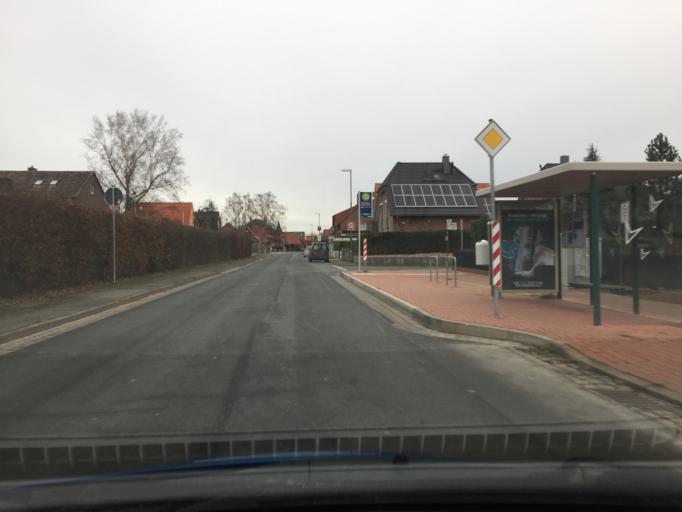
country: DE
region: Lower Saxony
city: Pattensen
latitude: 52.2879
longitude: 9.7664
